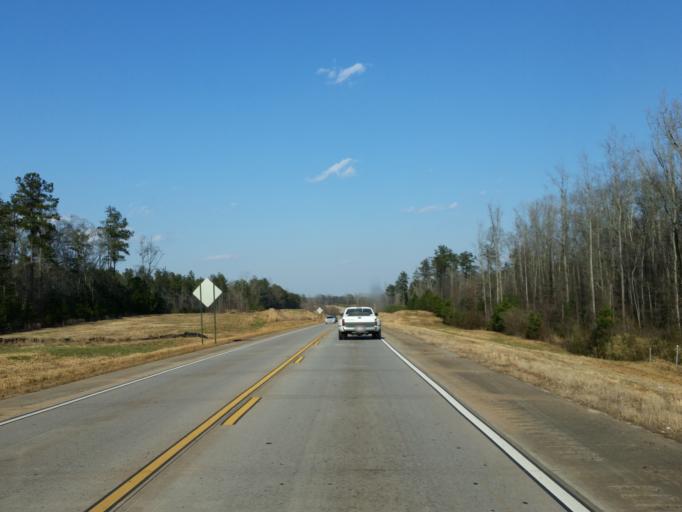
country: US
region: Georgia
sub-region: Lamar County
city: Barnesville
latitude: 33.0321
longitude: -84.1432
